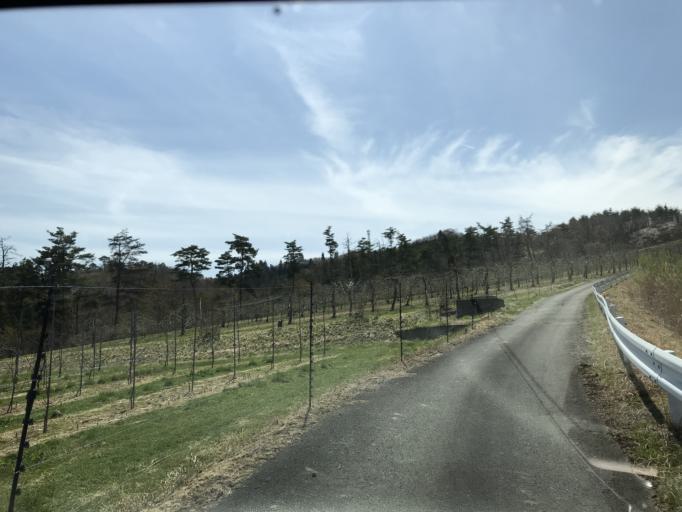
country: JP
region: Iwate
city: Ichinoseki
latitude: 38.8342
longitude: 141.2874
